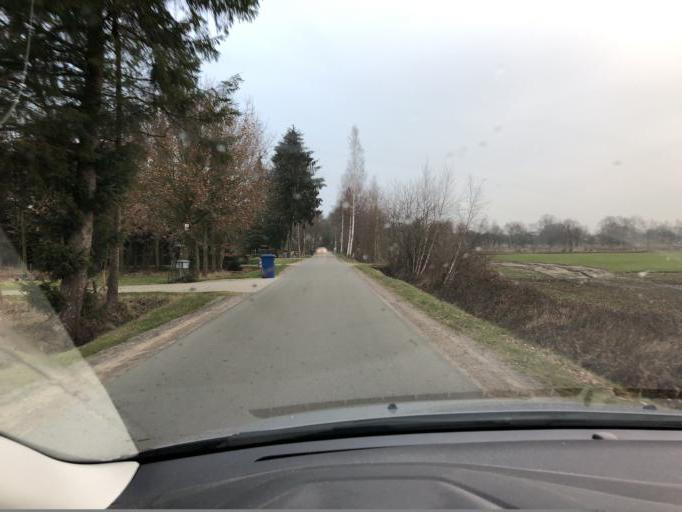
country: DE
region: Lower Saxony
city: Bad Zwischenahn
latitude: 53.1669
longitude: 8.0493
